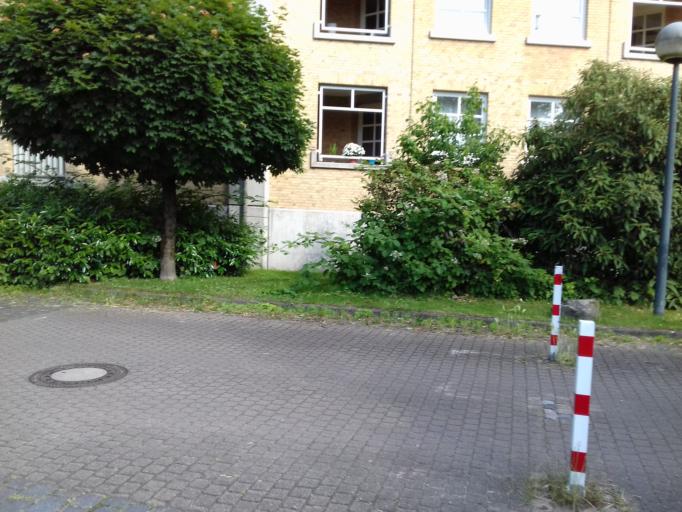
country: DE
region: Schleswig-Holstein
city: Neumunster
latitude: 54.0680
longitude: 9.9911
